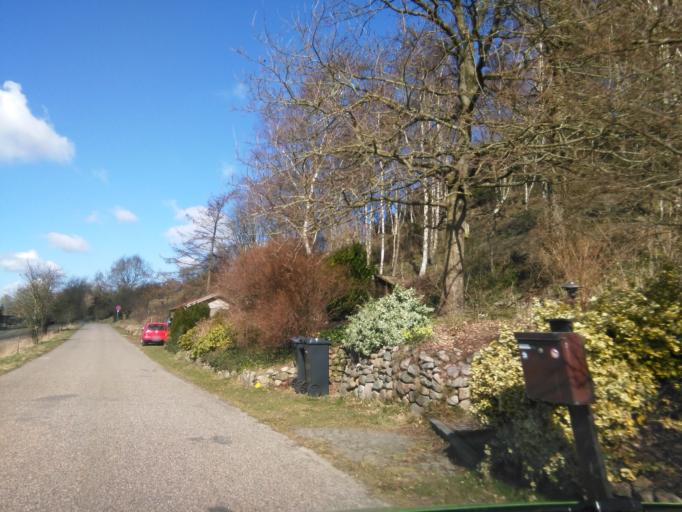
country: DK
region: Central Jutland
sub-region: Skanderborg Kommune
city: Ry
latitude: 56.1073
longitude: 9.7379
